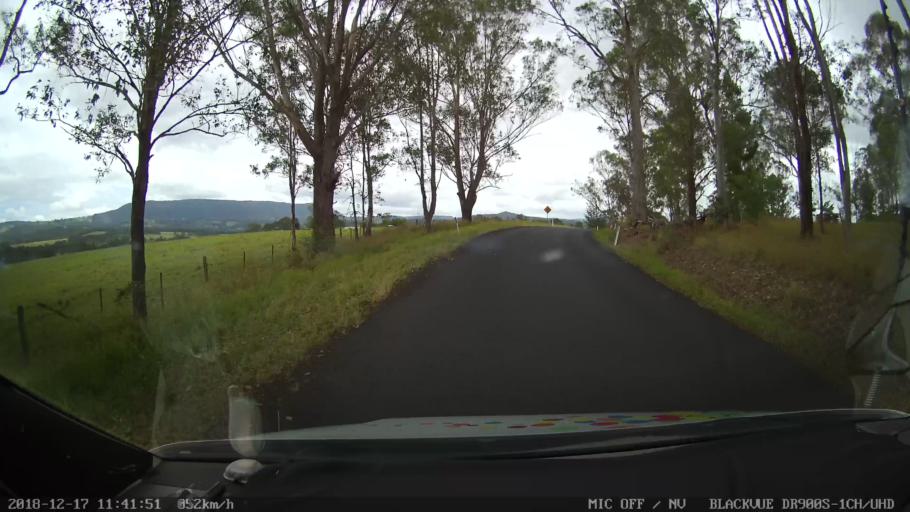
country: AU
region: New South Wales
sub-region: Kyogle
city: Kyogle
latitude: -28.6715
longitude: 152.5880
